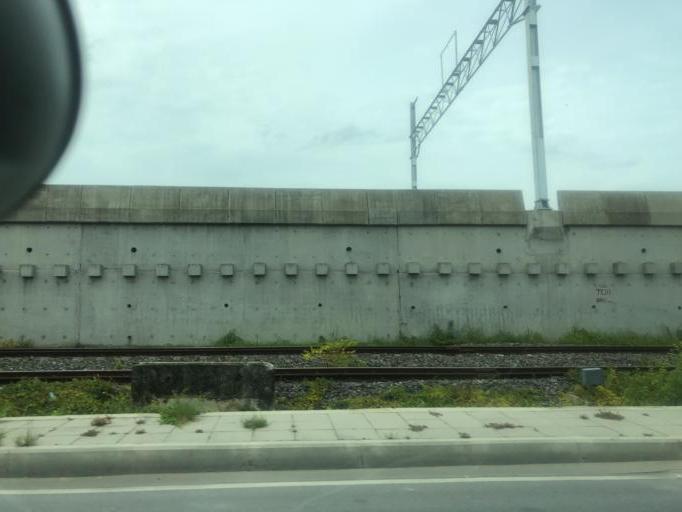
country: TH
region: Bangkok
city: Don Mueang
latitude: 13.9423
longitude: 100.6079
